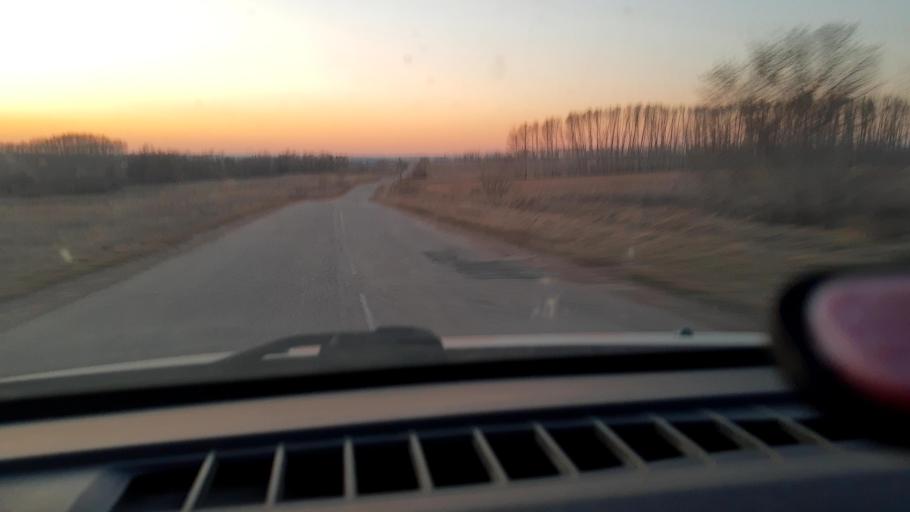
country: RU
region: Bashkortostan
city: Asanovo
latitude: 54.8261
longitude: 55.4664
